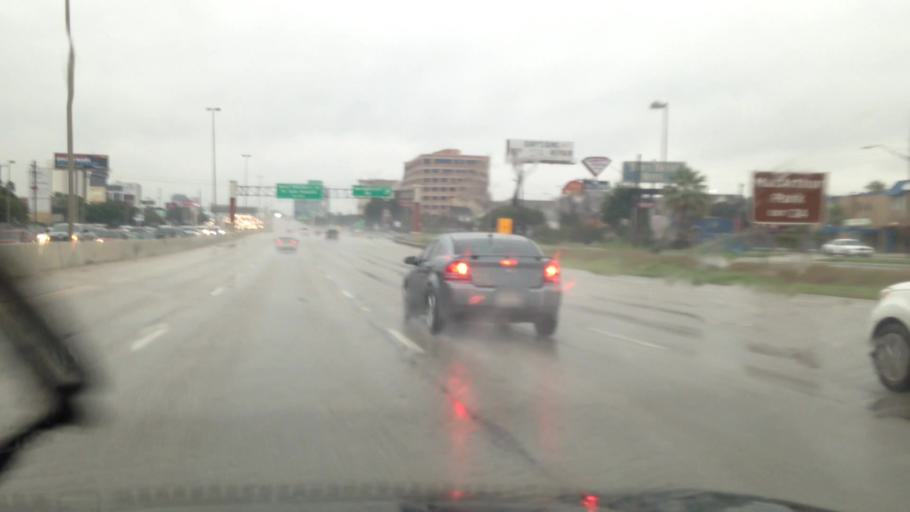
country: US
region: Texas
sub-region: Bexar County
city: Alamo Heights
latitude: 29.5164
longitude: -98.4613
